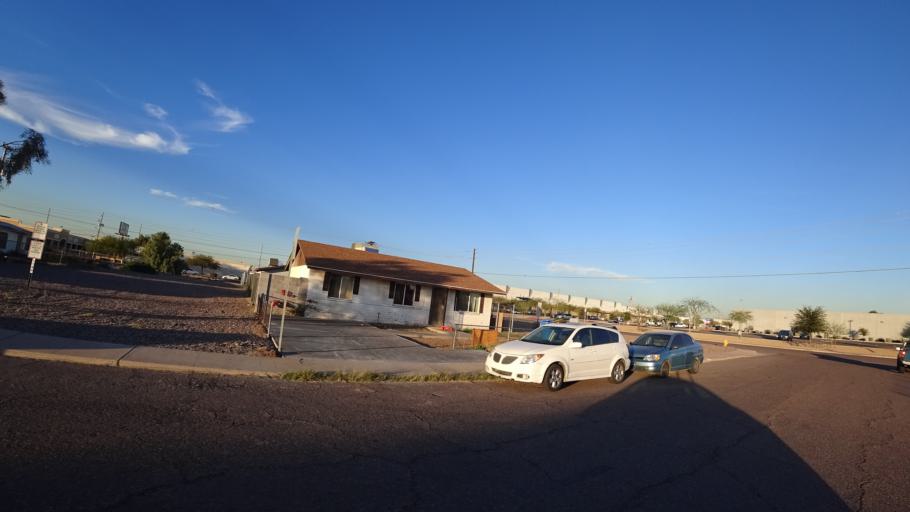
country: US
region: Arizona
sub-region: Maricopa County
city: Phoenix
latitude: 33.4359
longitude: -112.0570
